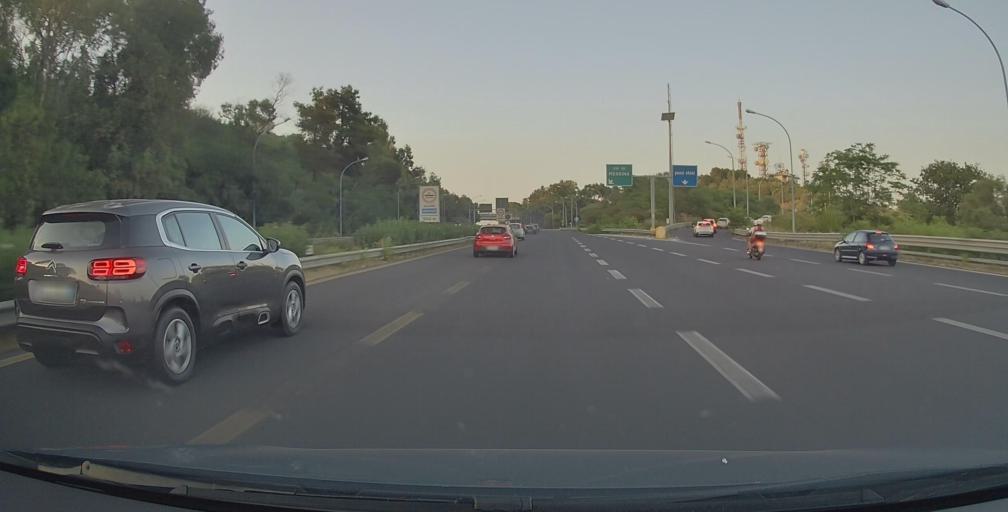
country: IT
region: Sicily
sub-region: Catania
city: San Gregorio di Catania
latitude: 37.5637
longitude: 15.0993
